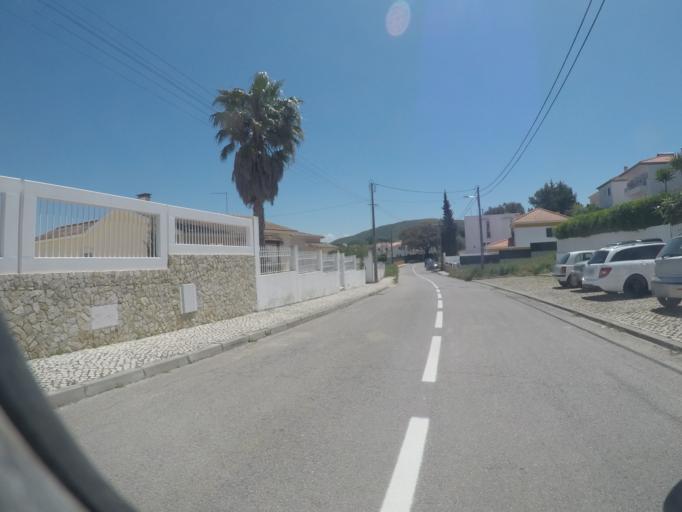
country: PT
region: Setubal
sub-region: Sesimbra
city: Sesimbra
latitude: 38.4618
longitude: -9.0765
